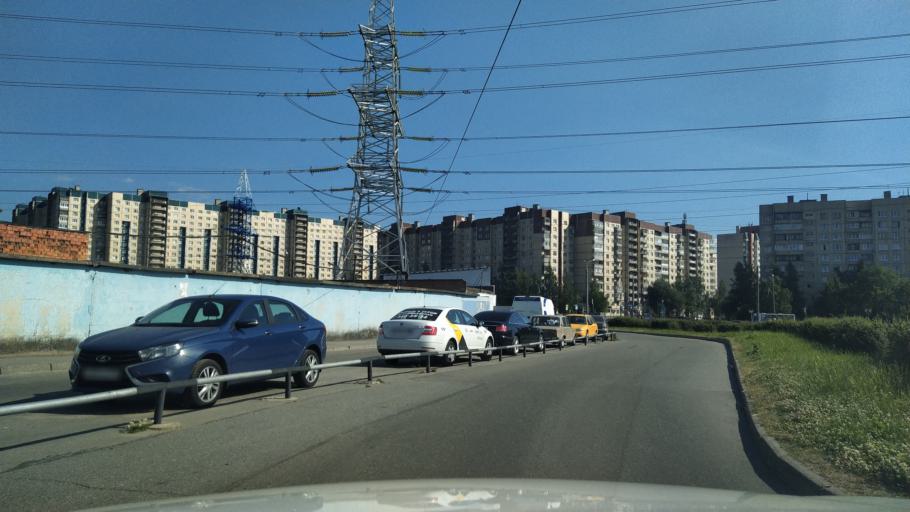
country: RU
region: St.-Petersburg
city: Uritsk
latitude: 59.8612
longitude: 30.2127
